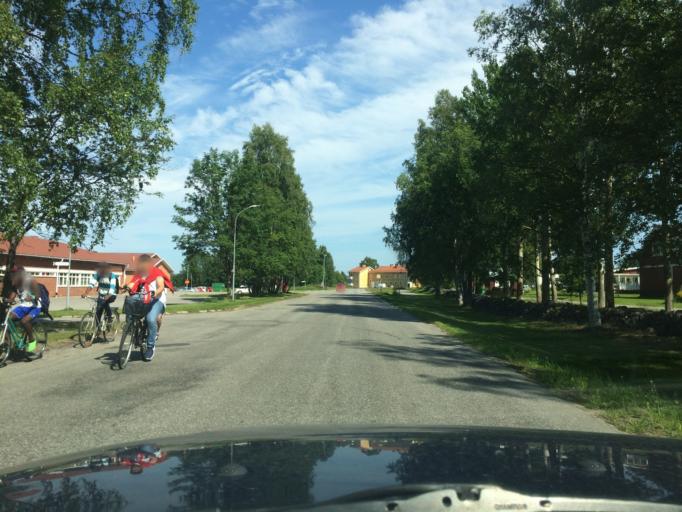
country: SE
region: Norrbotten
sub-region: Pitea Kommun
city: Bergsviken
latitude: 65.3466
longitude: 21.4107
